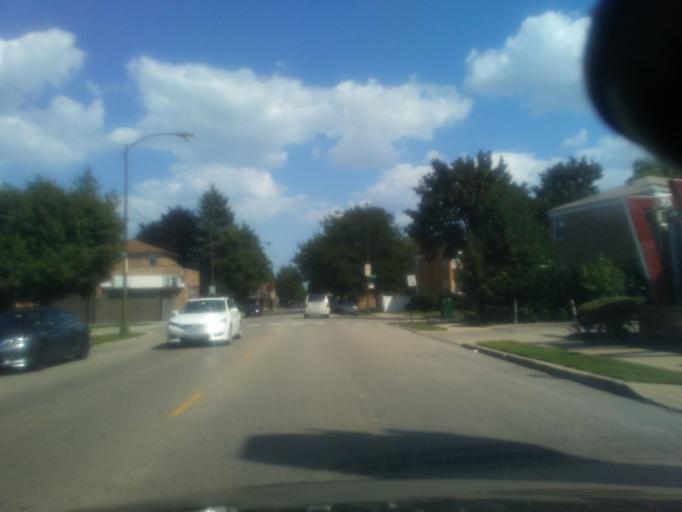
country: US
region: Illinois
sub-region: Cook County
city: Harwood Heights
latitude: 41.9729
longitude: -87.7775
